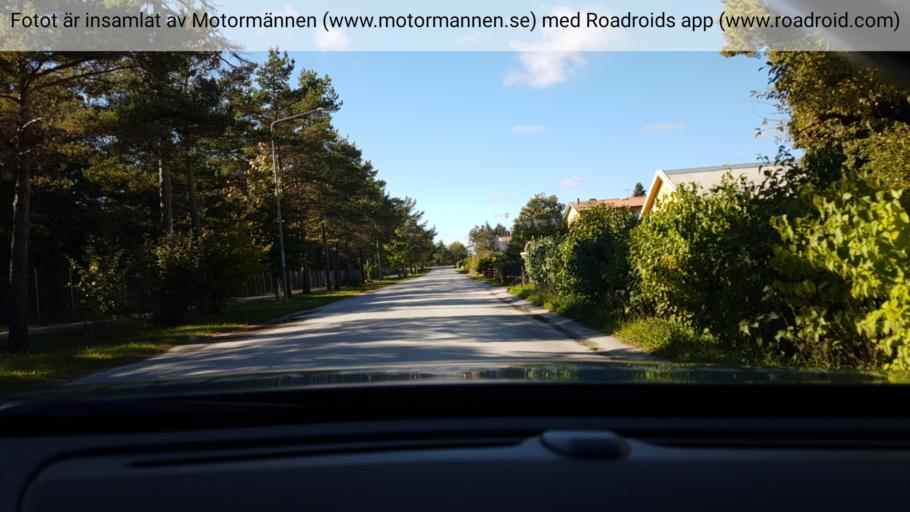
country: SE
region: Gotland
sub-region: Gotland
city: Slite
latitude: 57.7162
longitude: 18.7971
